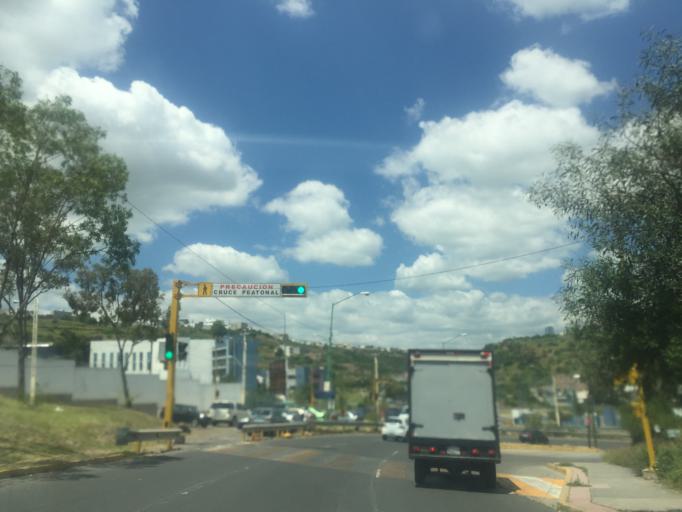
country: MX
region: Guanajuato
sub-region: Leon
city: La Ermita
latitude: 21.1408
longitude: -101.7190
